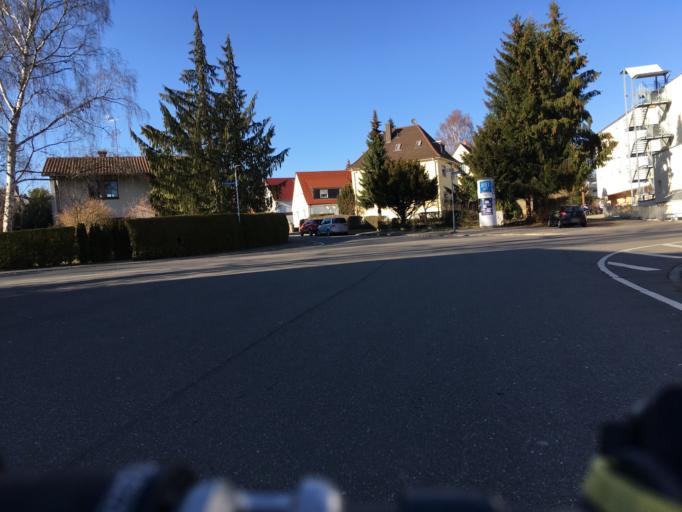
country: DE
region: Baden-Wuerttemberg
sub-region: Freiburg Region
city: Singen
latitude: 47.7696
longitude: 8.8319
